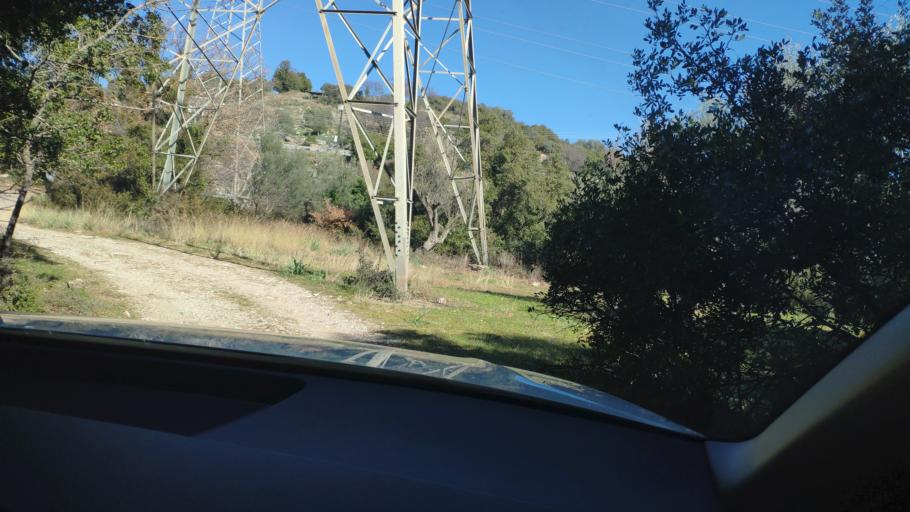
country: GR
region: West Greece
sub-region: Nomos Aitolias kai Akarnanias
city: Thermo
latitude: 38.5825
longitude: 21.6311
